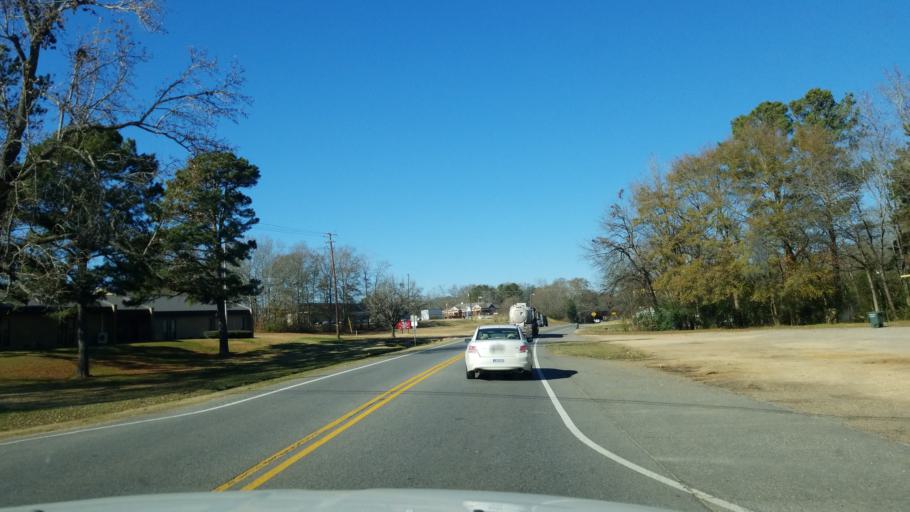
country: US
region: Alabama
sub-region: Pickens County
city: Gordo
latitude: 33.3199
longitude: -87.9086
